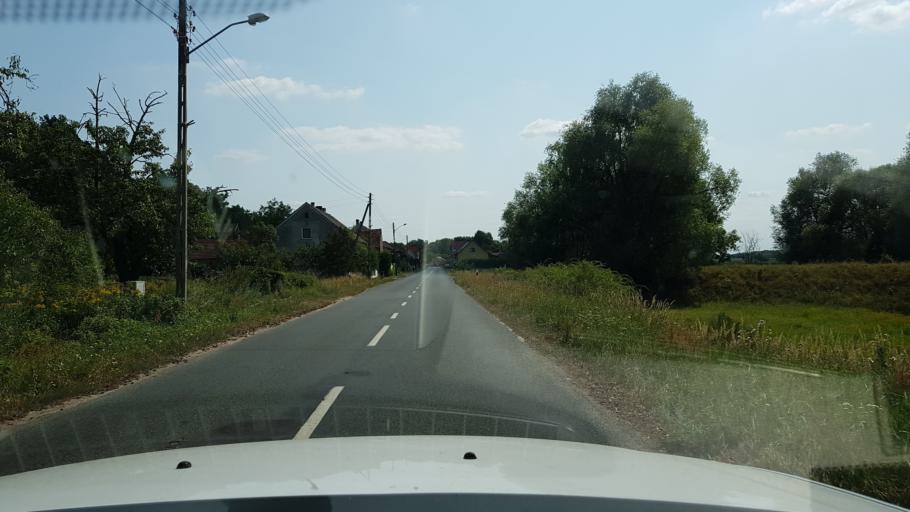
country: PL
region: West Pomeranian Voivodeship
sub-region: Powiat gryfinski
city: Cedynia
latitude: 52.8110
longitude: 14.2422
